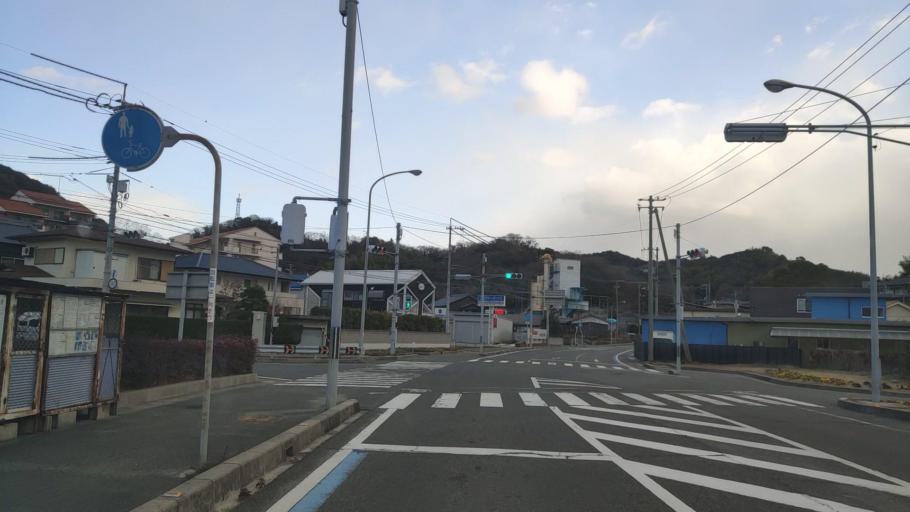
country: JP
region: Hiroshima
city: Innoshima
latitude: 34.2028
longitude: 133.1014
